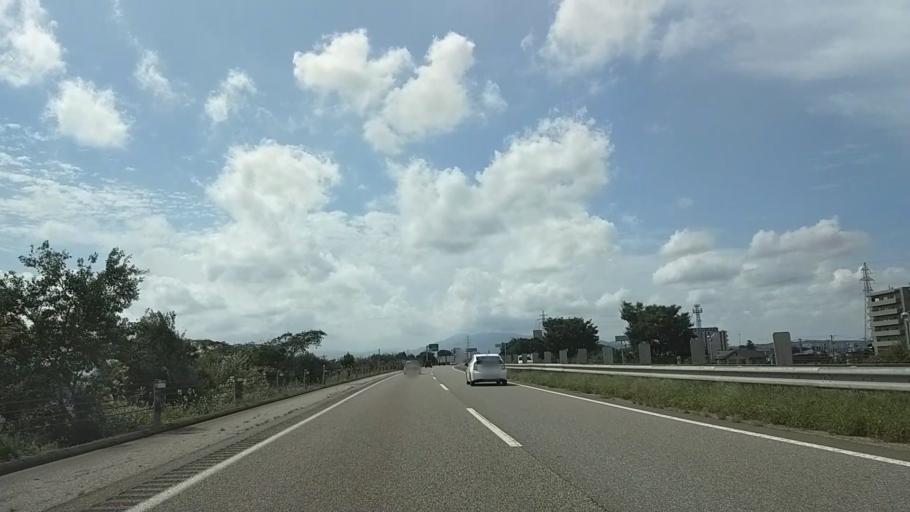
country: JP
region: Toyama
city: Nanto-shi
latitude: 36.6286
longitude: 136.9625
